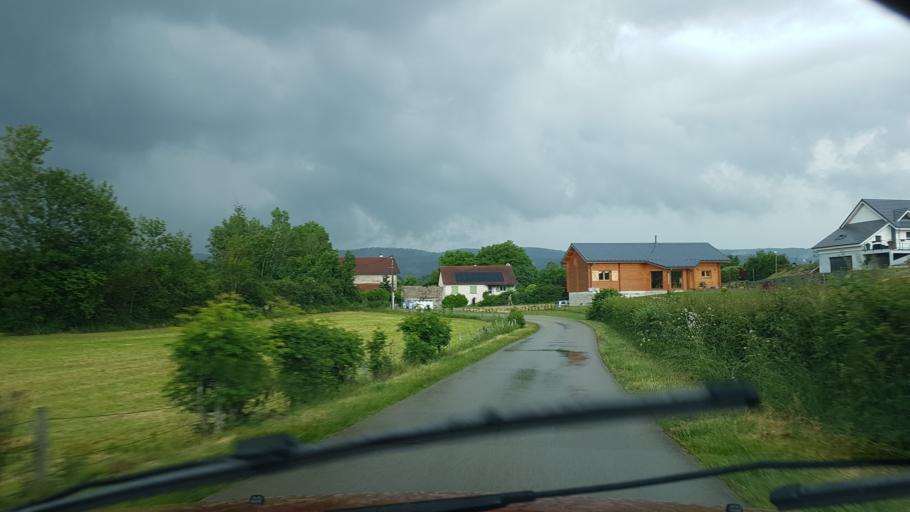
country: FR
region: Franche-Comte
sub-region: Departement du Jura
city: Clairvaux-les-Lacs
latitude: 46.5349
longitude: 5.7310
